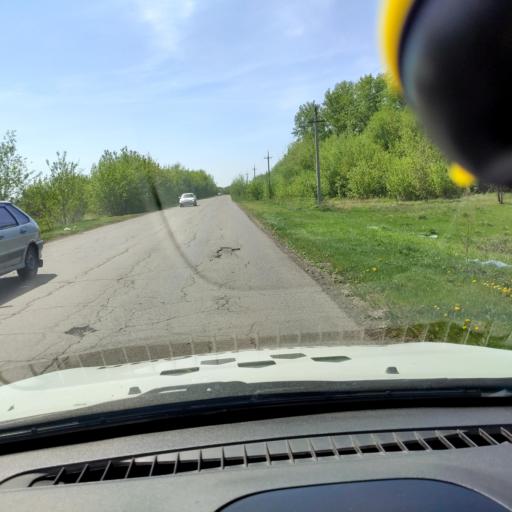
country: RU
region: Samara
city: Tol'yatti
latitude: 53.6427
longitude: 49.3157
